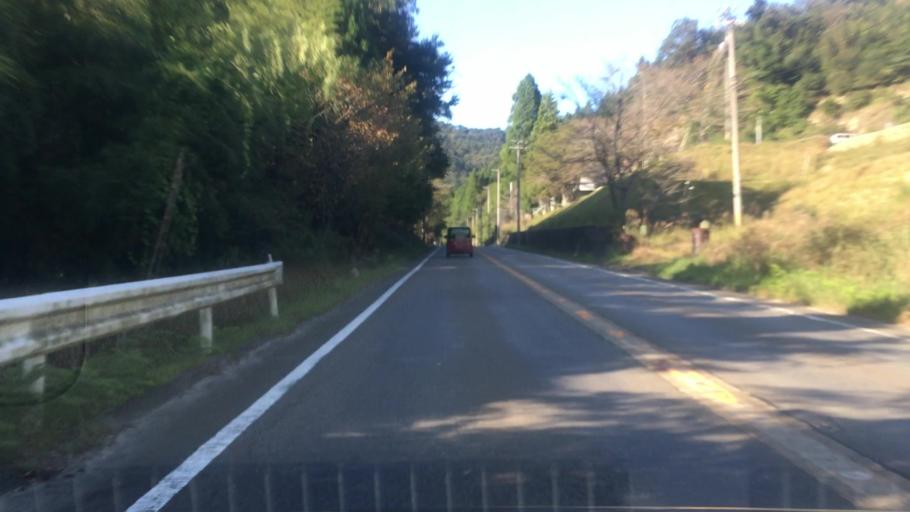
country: JP
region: Hyogo
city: Toyooka
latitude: 35.5666
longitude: 134.8528
